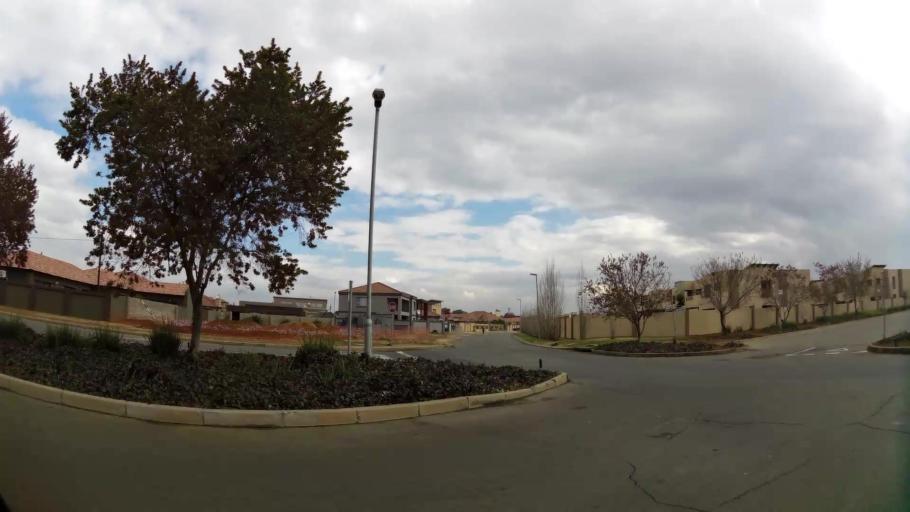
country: ZA
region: Gauteng
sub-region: Sedibeng District Municipality
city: Vanderbijlpark
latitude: -26.7269
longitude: 27.8661
